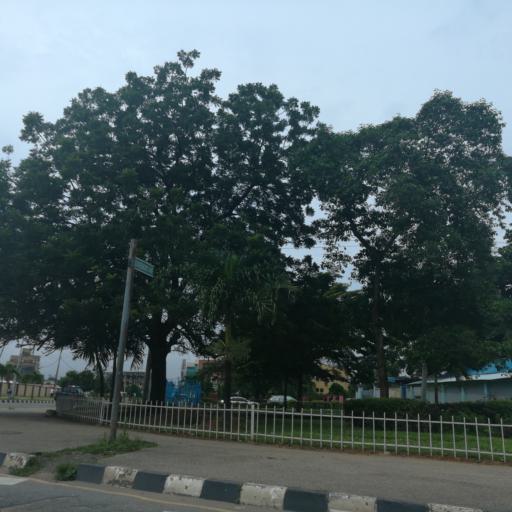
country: NG
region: Lagos
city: Ikeja
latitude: 6.6131
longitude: 3.3601
